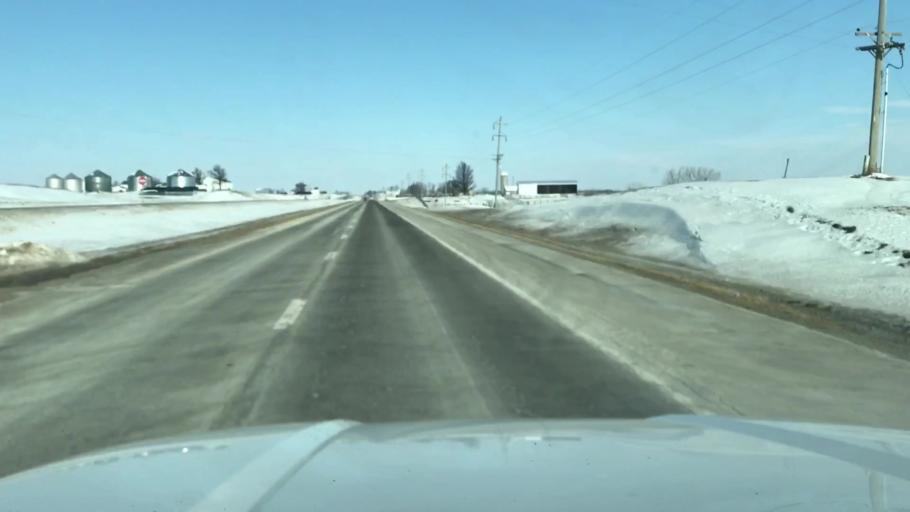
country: US
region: Missouri
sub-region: Nodaway County
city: Maryville
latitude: 40.2392
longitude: -94.8673
